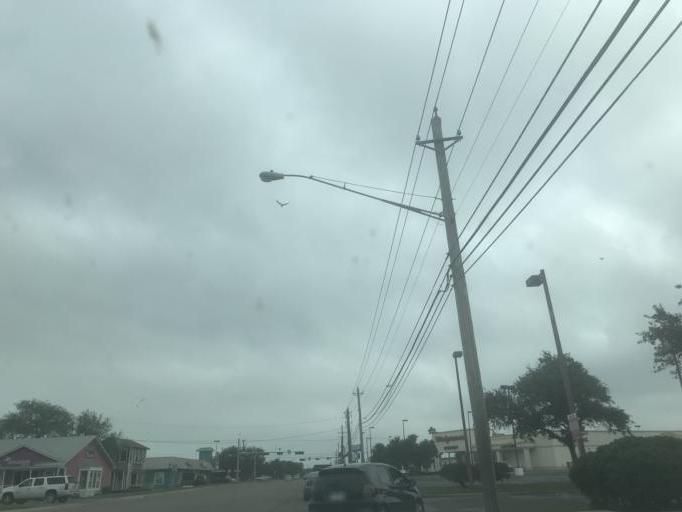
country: US
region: Texas
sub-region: Nueces County
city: Corpus Christi
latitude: 27.7089
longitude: -97.3641
